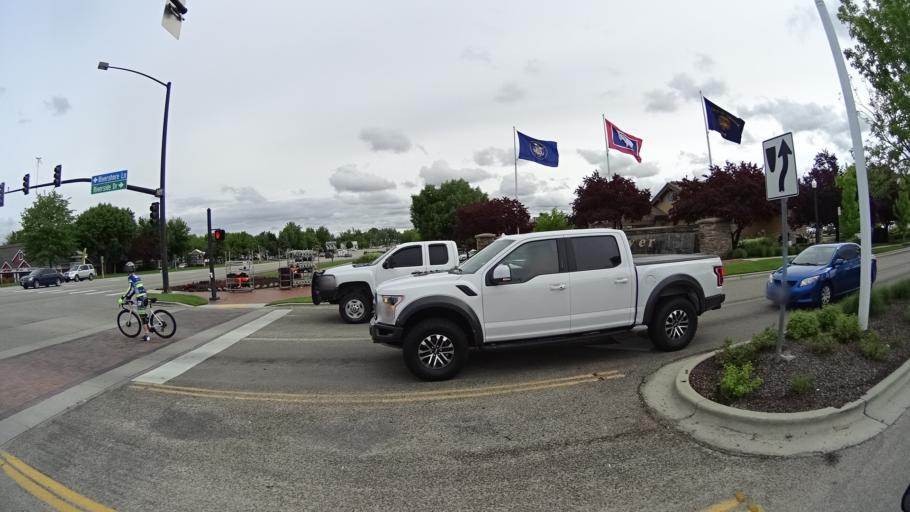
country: US
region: Idaho
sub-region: Ada County
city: Eagle
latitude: 43.6878
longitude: -116.3538
